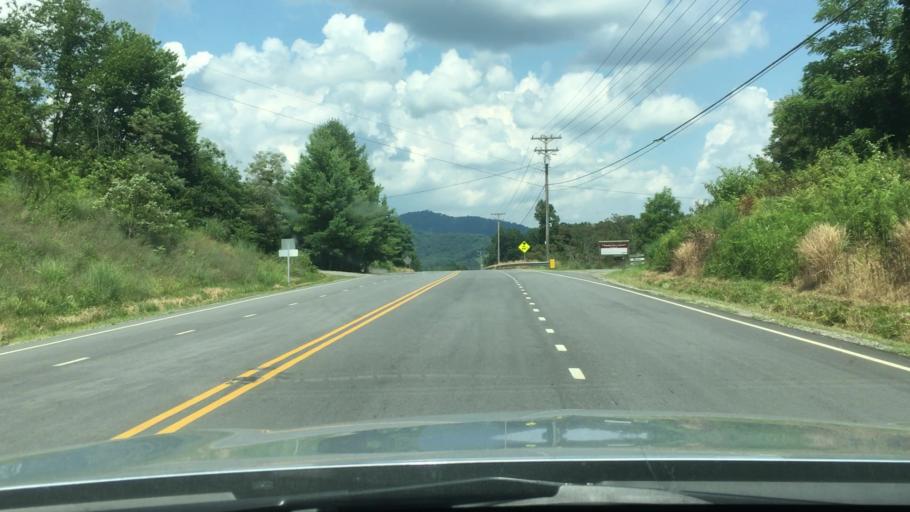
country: US
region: North Carolina
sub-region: Madison County
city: Marshall
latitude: 35.8219
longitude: -82.6335
